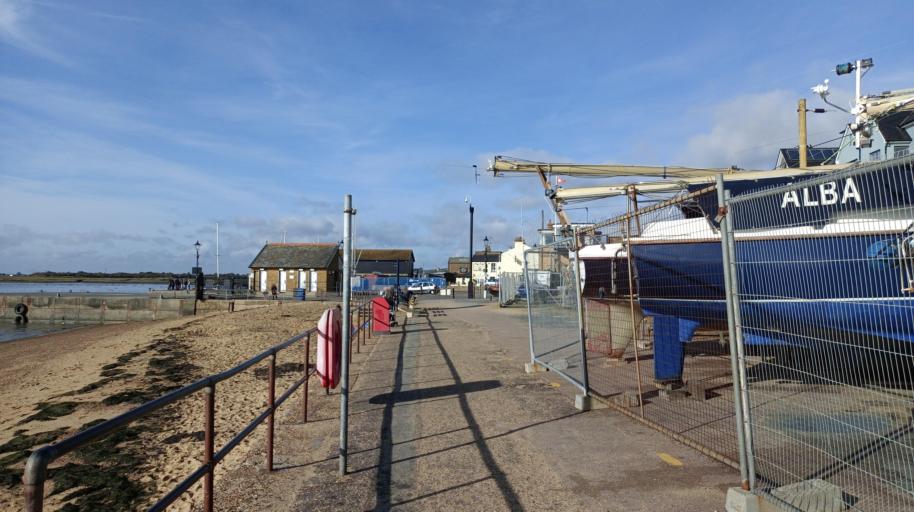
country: GB
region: England
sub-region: Southend-on-Sea
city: Leigh-on-Sea
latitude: 51.5394
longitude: 0.6535
